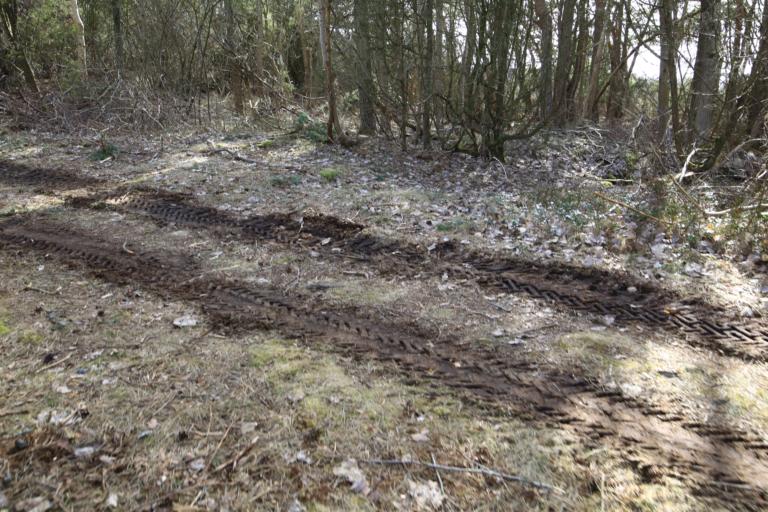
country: SE
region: Halland
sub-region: Kungsbacka Kommun
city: Frillesas
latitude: 57.2712
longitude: 12.1148
